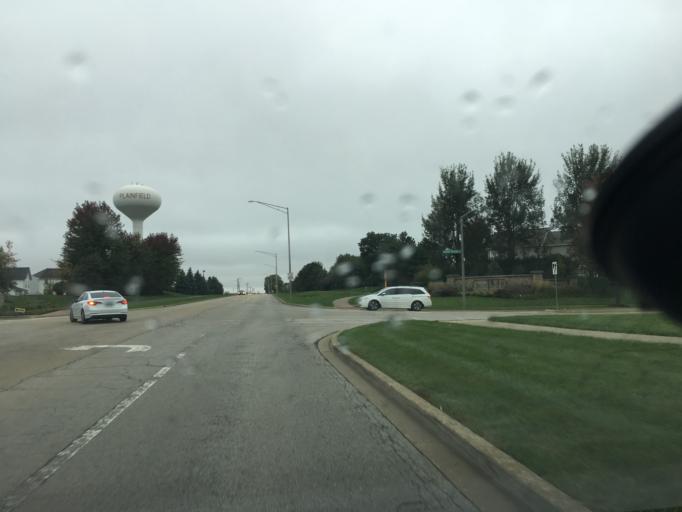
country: US
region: Illinois
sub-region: Will County
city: Plainfield
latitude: 41.6662
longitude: -88.2091
